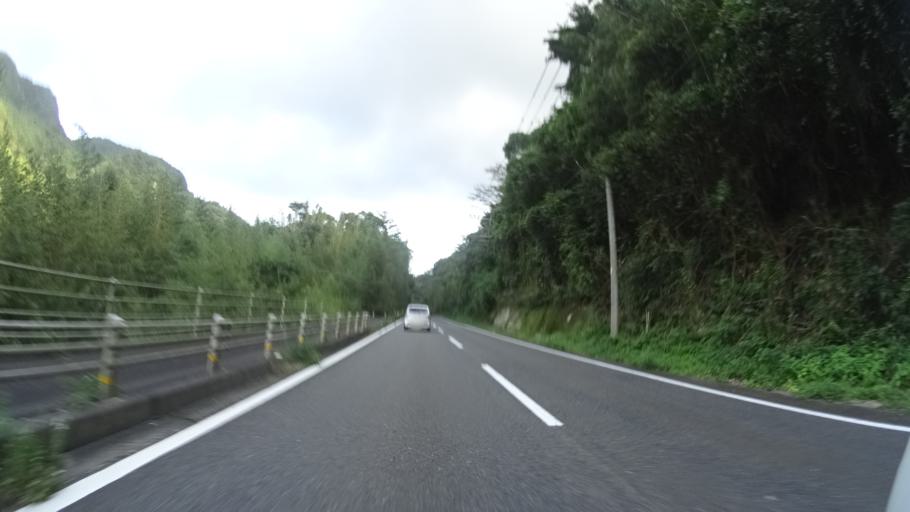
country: JP
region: Oita
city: Beppu
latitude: 33.3530
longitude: 131.3985
